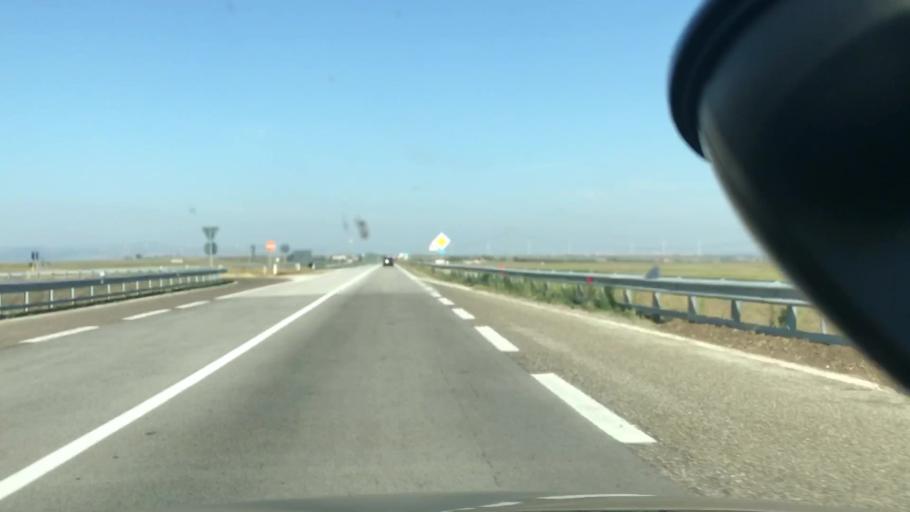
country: IT
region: Basilicate
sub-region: Provincia di Potenza
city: Venosa
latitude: 40.9942
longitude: 15.8871
